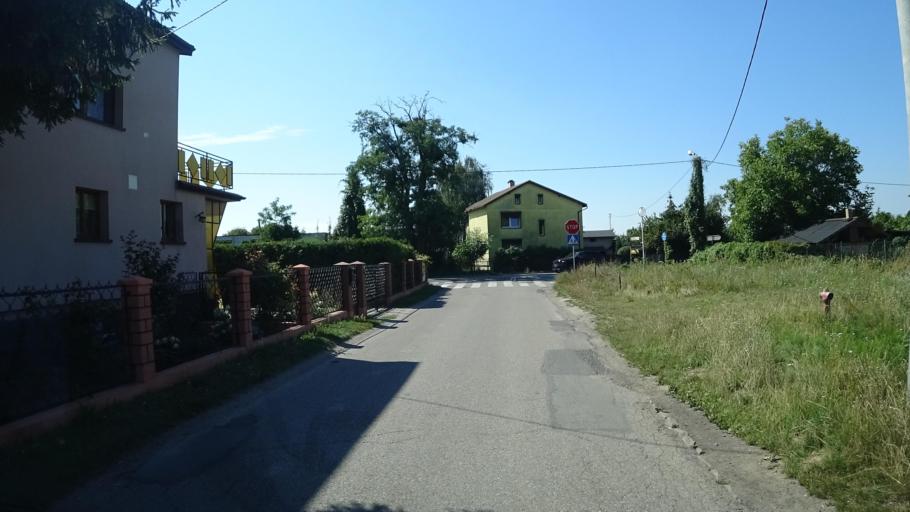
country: PL
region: Greater Poland Voivodeship
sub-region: Powiat koninski
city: Slesin
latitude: 52.3730
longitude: 18.3227
